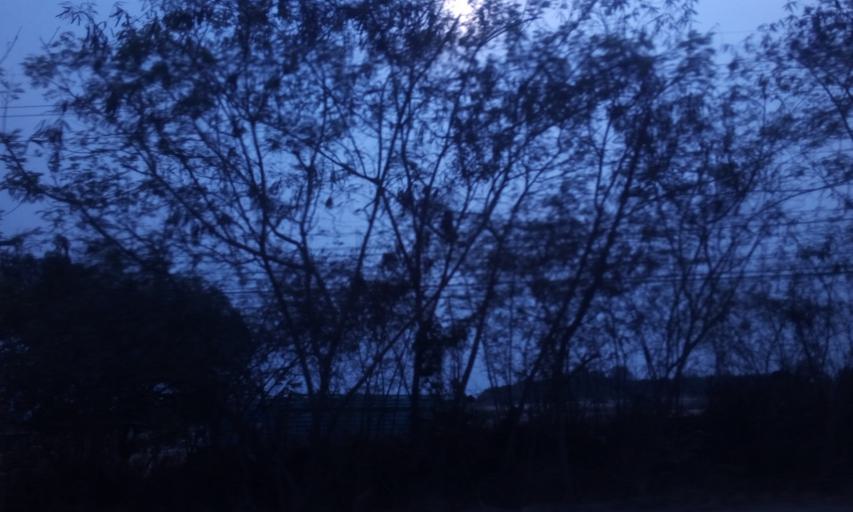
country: TH
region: Chachoengsao
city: Plaeng Yao
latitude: 13.5264
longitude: 101.2640
